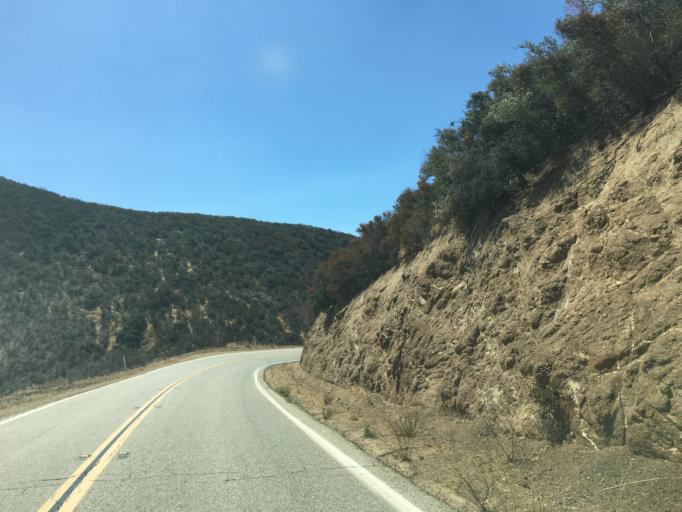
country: US
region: California
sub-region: Los Angeles County
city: Green Valley
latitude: 34.6004
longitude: -118.3844
